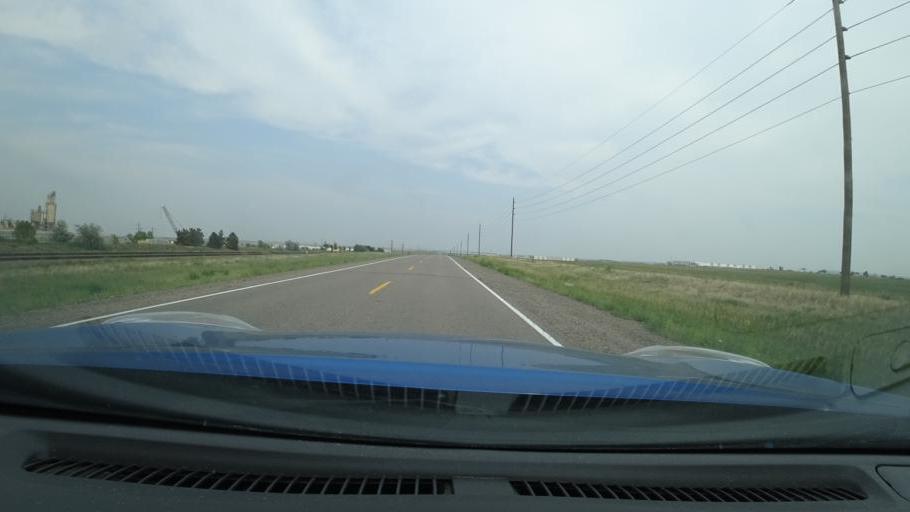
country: US
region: Colorado
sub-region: Adams County
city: Aurora
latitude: 39.7511
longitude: -104.7426
